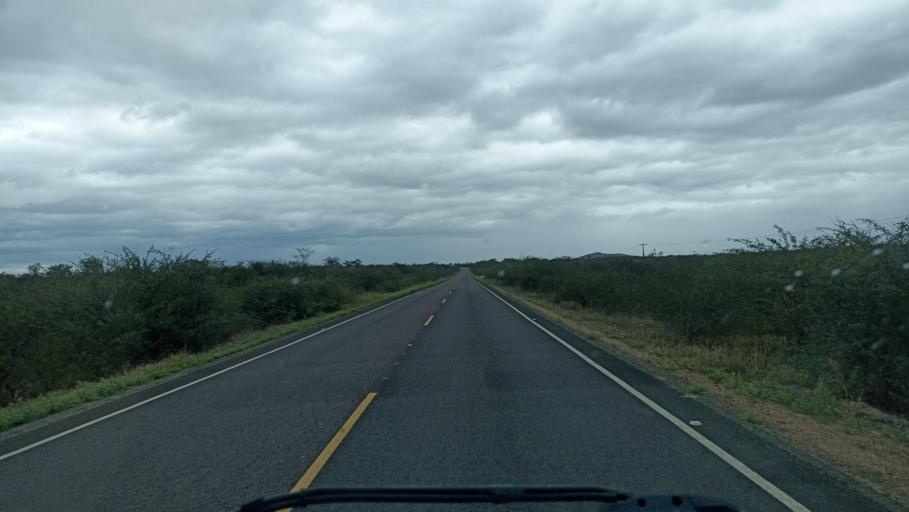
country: BR
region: Bahia
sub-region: Iacu
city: Iacu
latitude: -12.9743
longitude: -40.5089
